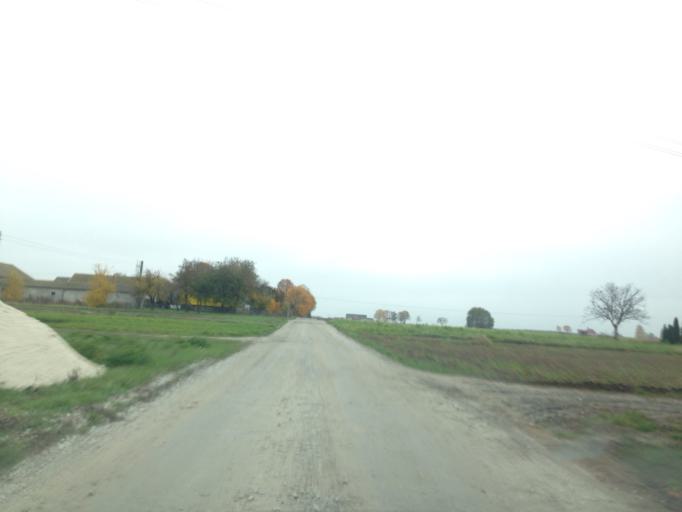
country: PL
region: Kujawsko-Pomorskie
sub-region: Powiat brodnicki
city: Bartniczka
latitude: 53.2127
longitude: 19.5668
